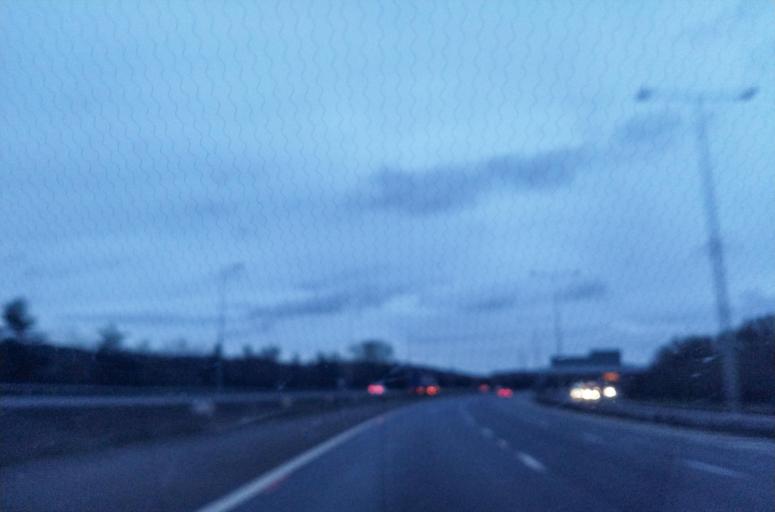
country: GB
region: England
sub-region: Kent
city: Boxley
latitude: 51.2991
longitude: 0.5191
